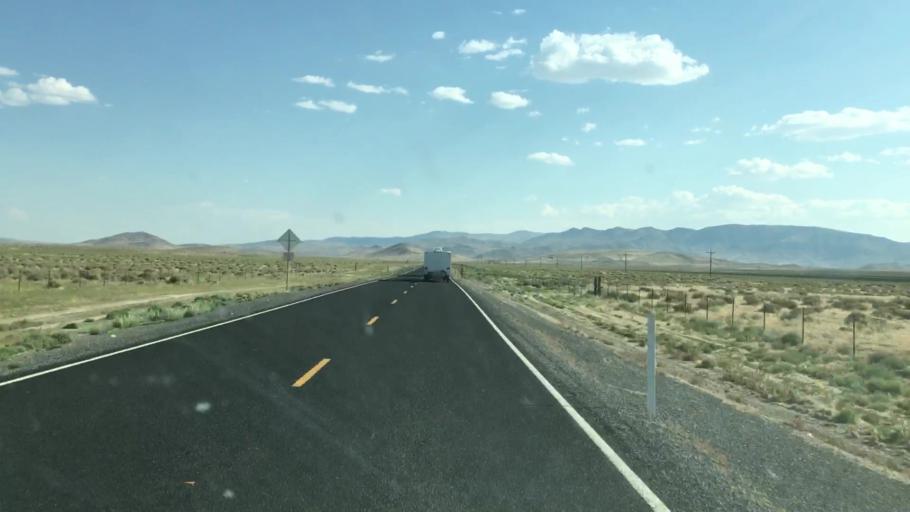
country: US
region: Nevada
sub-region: Lyon County
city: Fernley
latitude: 39.6701
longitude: -119.3321
